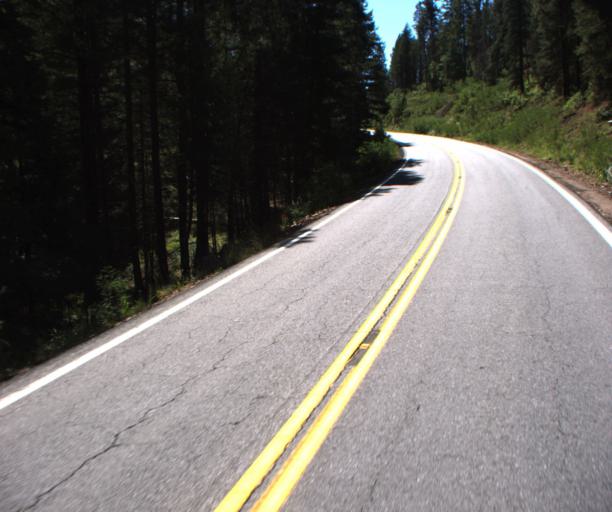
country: US
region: Arizona
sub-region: Apache County
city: Eagar
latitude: 33.7357
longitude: -109.2077
